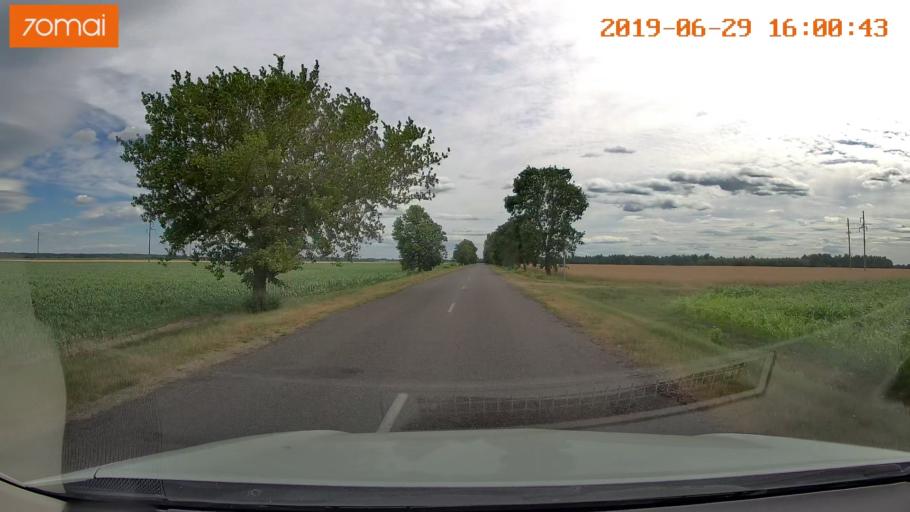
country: BY
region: Brest
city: Luninyets
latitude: 52.2567
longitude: 27.0172
